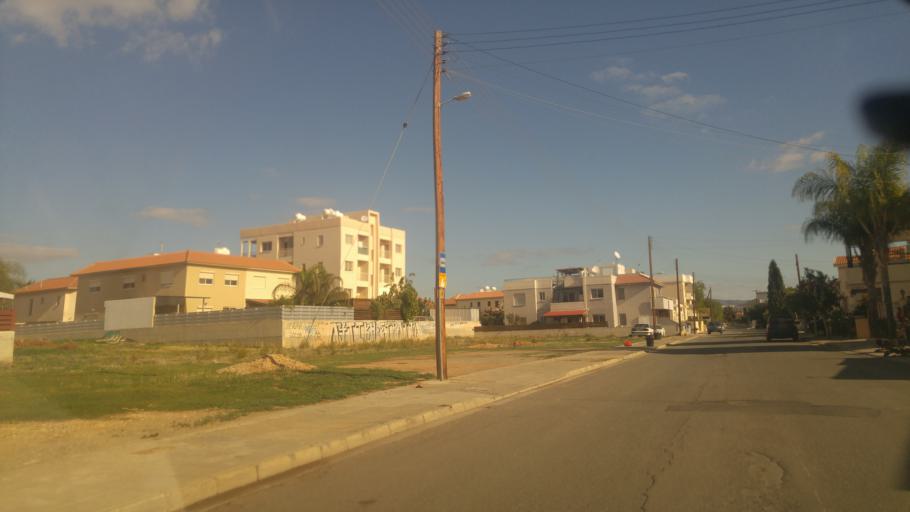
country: CY
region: Limassol
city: Ypsonas
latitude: 34.6872
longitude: 32.9646
